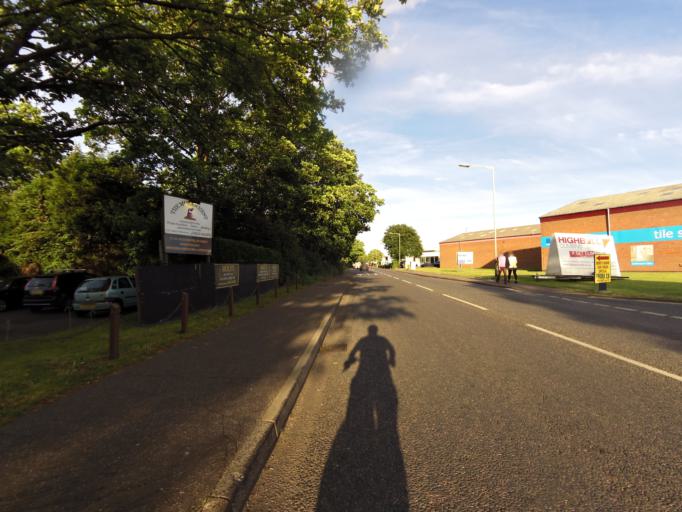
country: GB
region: England
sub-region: Norfolk
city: Norwich
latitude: 52.6654
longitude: 1.2802
